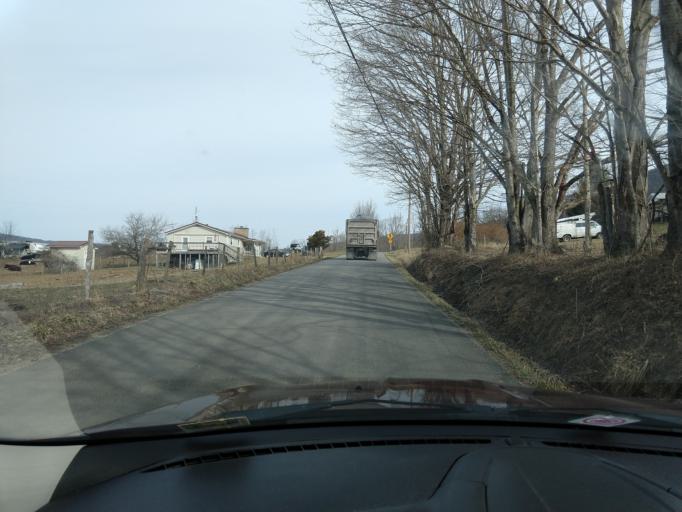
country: US
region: West Virginia
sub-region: Tucker County
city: Parsons
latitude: 39.0163
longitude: -79.5115
